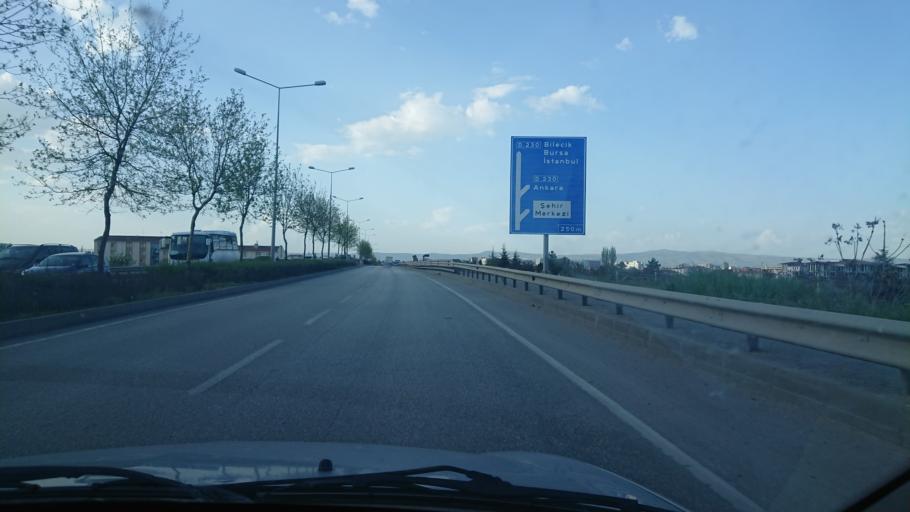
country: TR
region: Eskisehir
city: Eskisehir
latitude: 39.7734
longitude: 30.4839
